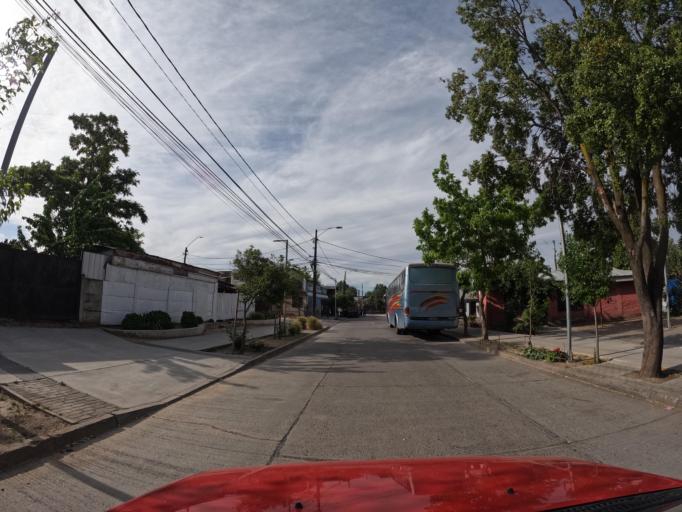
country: CL
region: Maule
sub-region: Provincia de Talca
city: Talca
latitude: -35.4408
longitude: -71.6603
